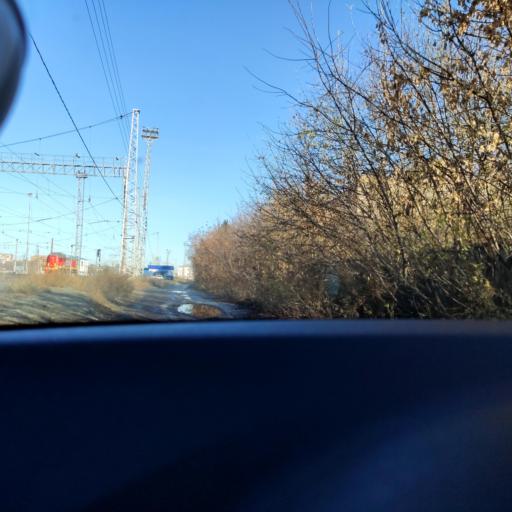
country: RU
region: Samara
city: Samara
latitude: 53.2078
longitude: 50.2585
